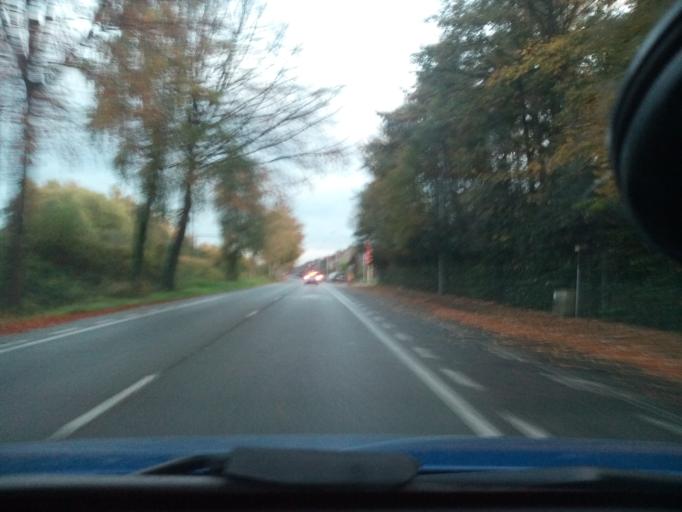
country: BE
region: Flanders
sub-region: Provincie West-Vlaanderen
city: Brugge
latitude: 51.1833
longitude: 3.2247
